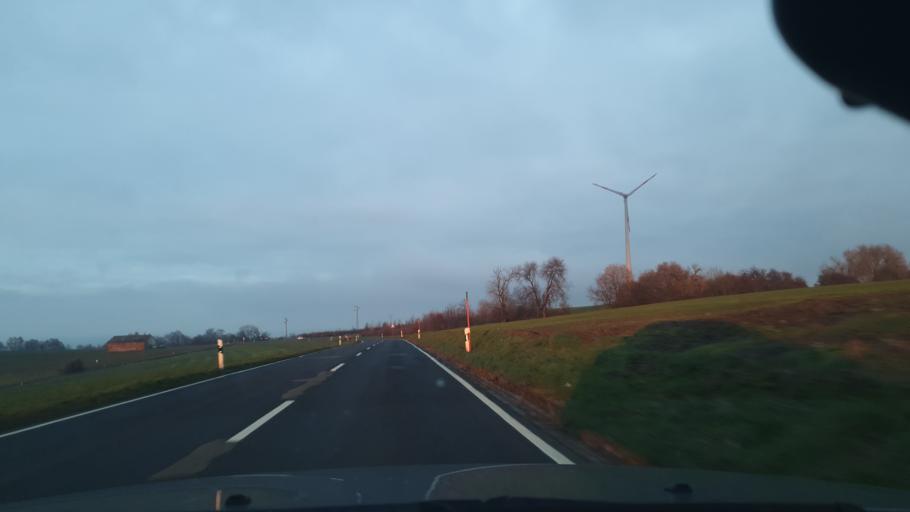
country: DE
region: Rheinland-Pfalz
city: Langwieden
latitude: 49.3747
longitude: 7.5098
